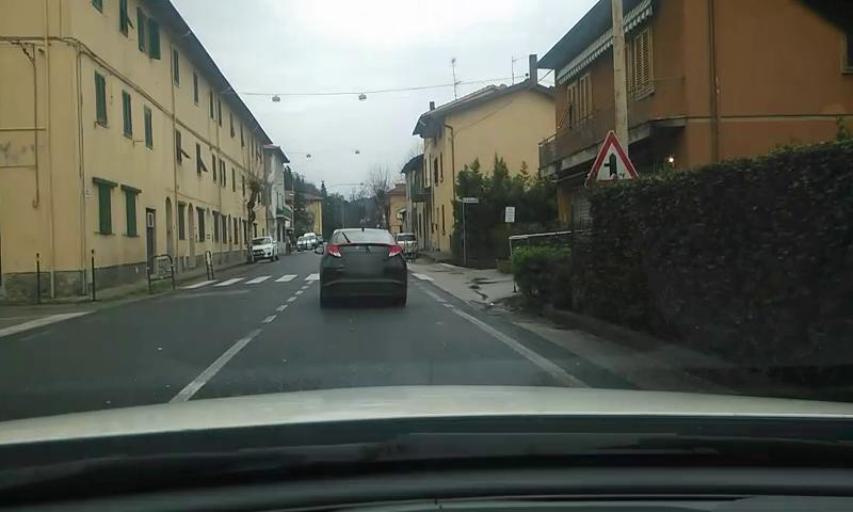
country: IT
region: Tuscany
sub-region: Provincia di Prato
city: Vaiano
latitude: 43.9461
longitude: 11.1246
